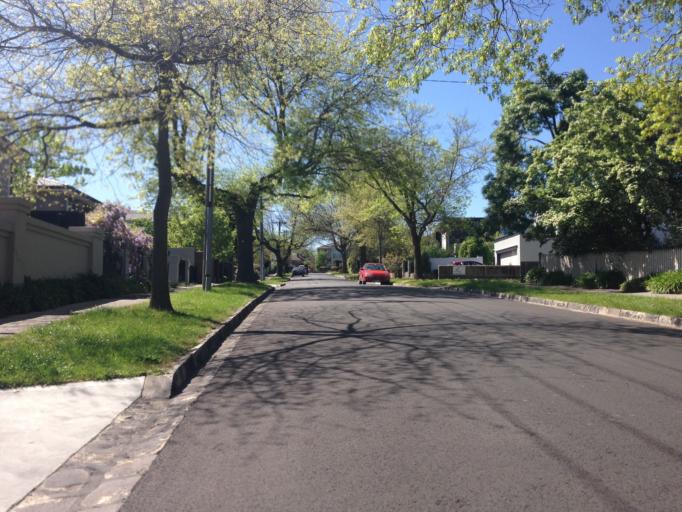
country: AU
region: Victoria
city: Balwyn
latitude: -37.8035
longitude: 145.0673
